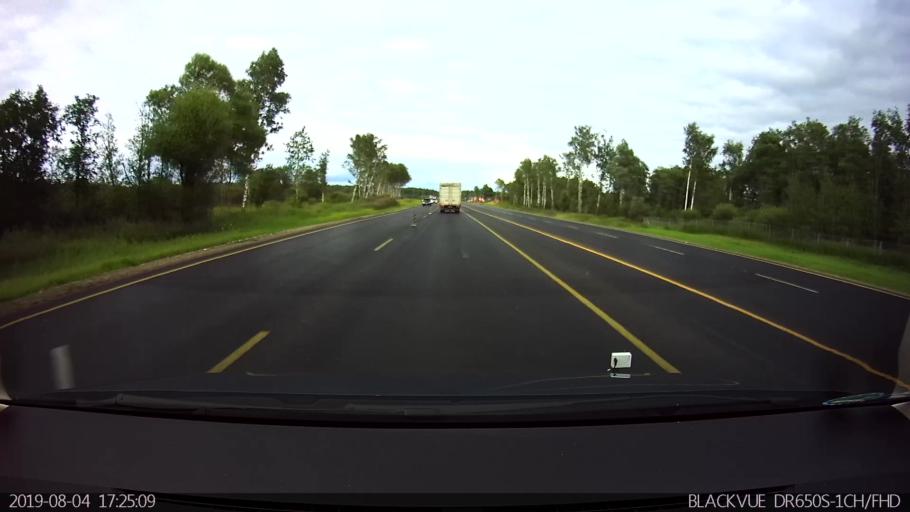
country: RU
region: Smolensk
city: Gagarin
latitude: 55.4883
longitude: 34.9537
